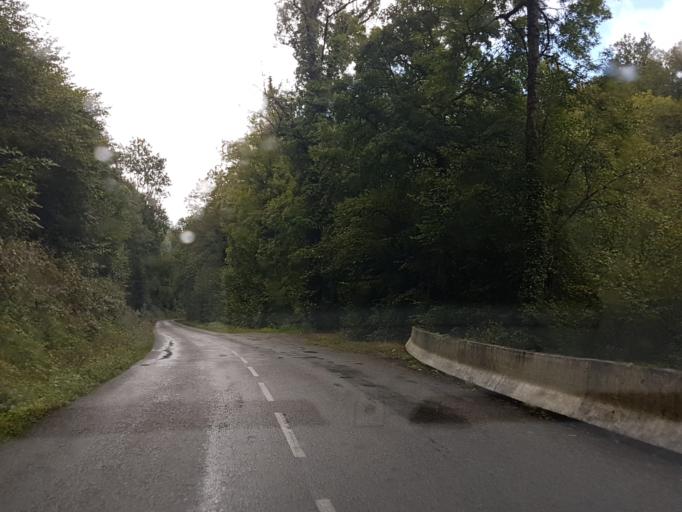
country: FR
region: Midi-Pyrenees
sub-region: Departement de l'Ariege
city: Saint-Girons
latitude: 42.9012
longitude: 1.2250
